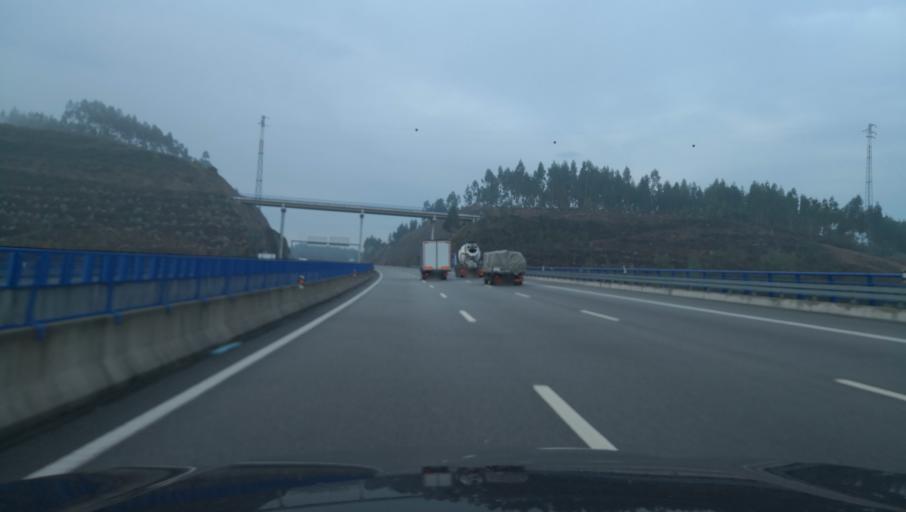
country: PT
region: Porto
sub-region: Paredes
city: Recarei
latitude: 41.1273
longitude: -8.4317
